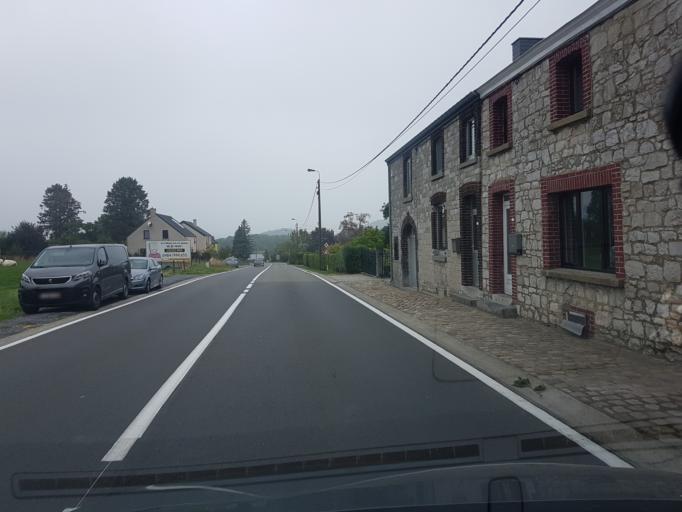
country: BE
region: Wallonia
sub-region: Province de Namur
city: Andenne
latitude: 50.4831
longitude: 5.1068
